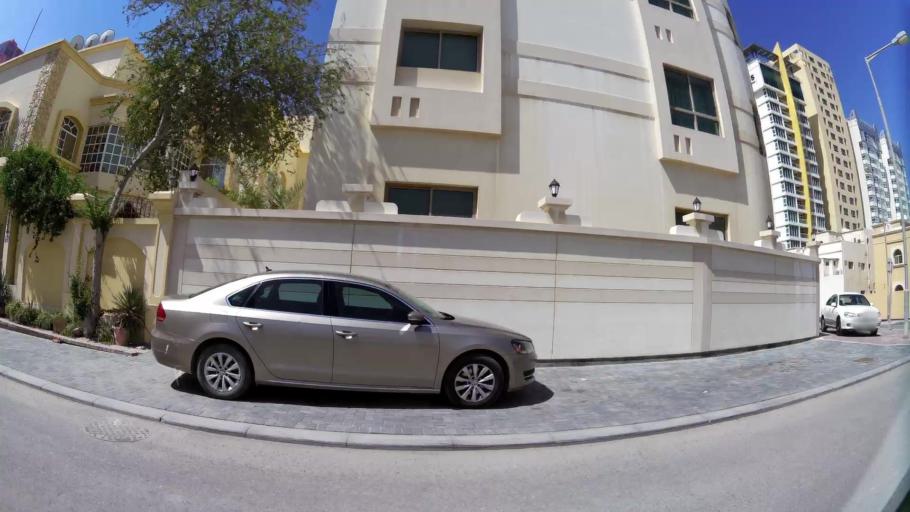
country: BH
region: Manama
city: Manama
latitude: 26.2185
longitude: 50.6129
